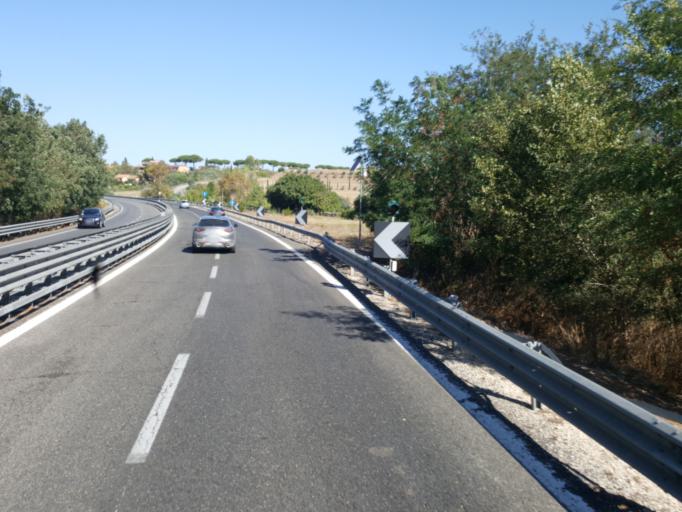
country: IT
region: Latium
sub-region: Provincia di Viterbo
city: Montalto di Castro
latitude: 42.3531
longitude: 11.5975
